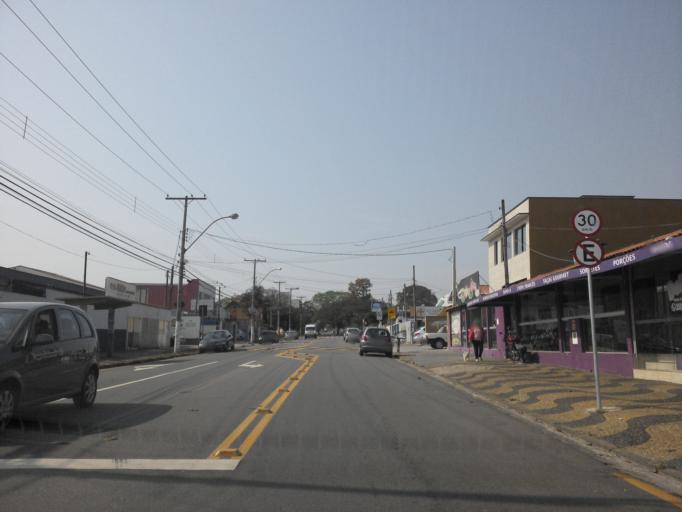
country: BR
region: Sao Paulo
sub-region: Campinas
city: Campinas
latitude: -22.9213
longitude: -47.0835
